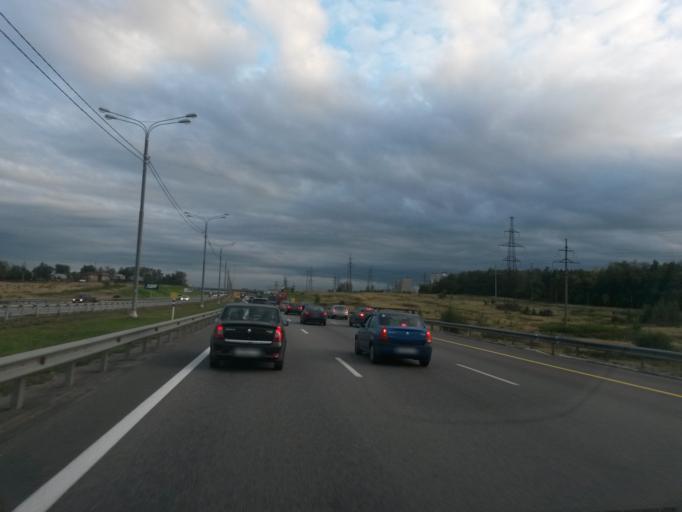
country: RU
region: Moskovskaya
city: Vostryakovo
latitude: 55.3845
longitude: 37.7762
